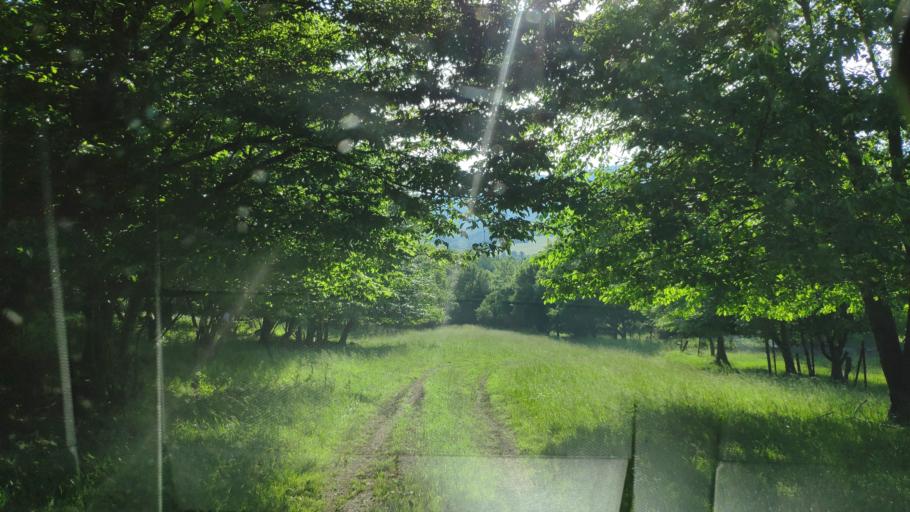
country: SK
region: Presovsky
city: Vranov nad Topl'ou
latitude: 48.8249
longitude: 21.5805
